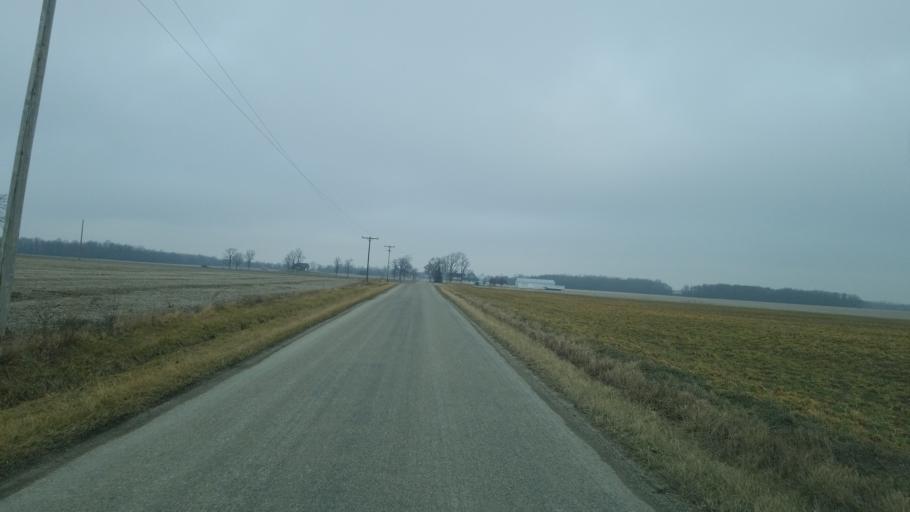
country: US
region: Indiana
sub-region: Adams County
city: Berne
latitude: 40.6870
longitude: -84.8550
